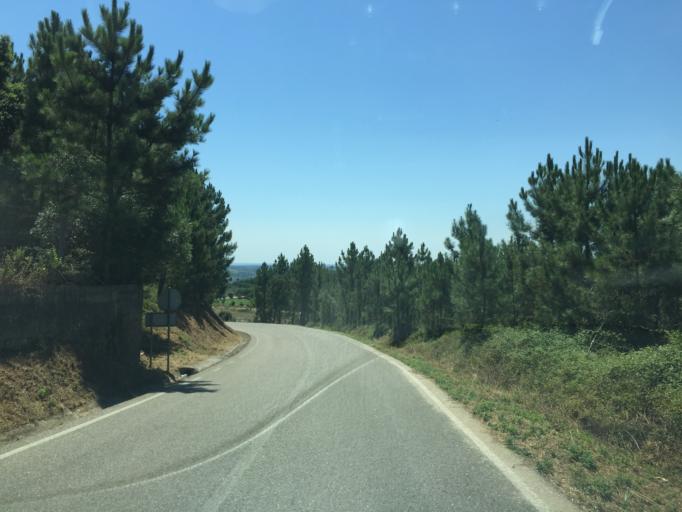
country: PT
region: Santarem
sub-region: Ferreira do Zezere
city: Ferreira do Zezere
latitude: 39.5974
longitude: -8.3011
